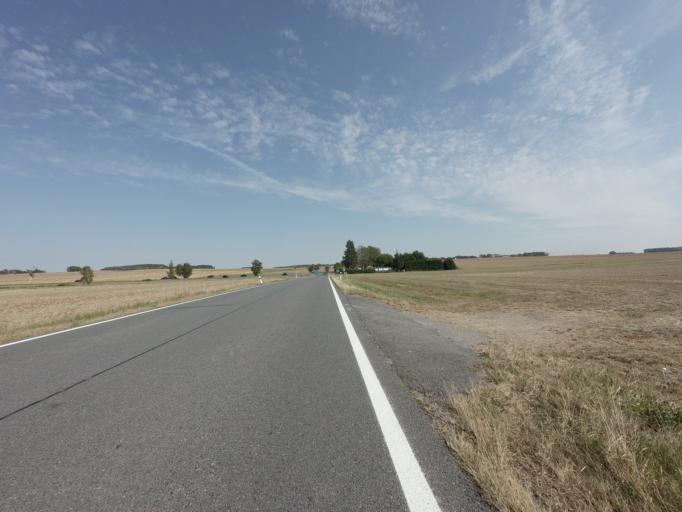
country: CZ
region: Jihocesky
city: Bernartice
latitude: 49.3738
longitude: 14.3794
